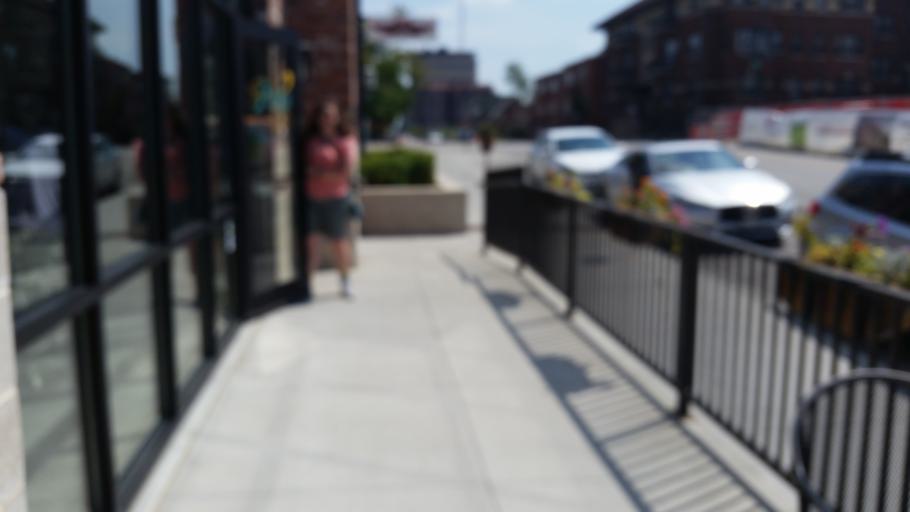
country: US
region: Nebraska
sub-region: Douglas County
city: Omaha
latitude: 41.2579
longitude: -95.9724
